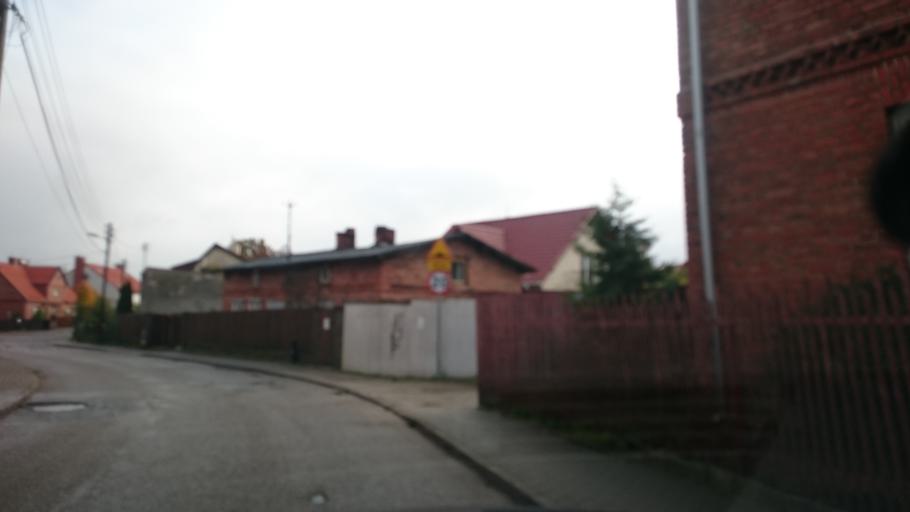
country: PL
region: Pomeranian Voivodeship
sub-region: Gdynia
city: Wielki Kack
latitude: 54.4688
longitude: 18.4943
